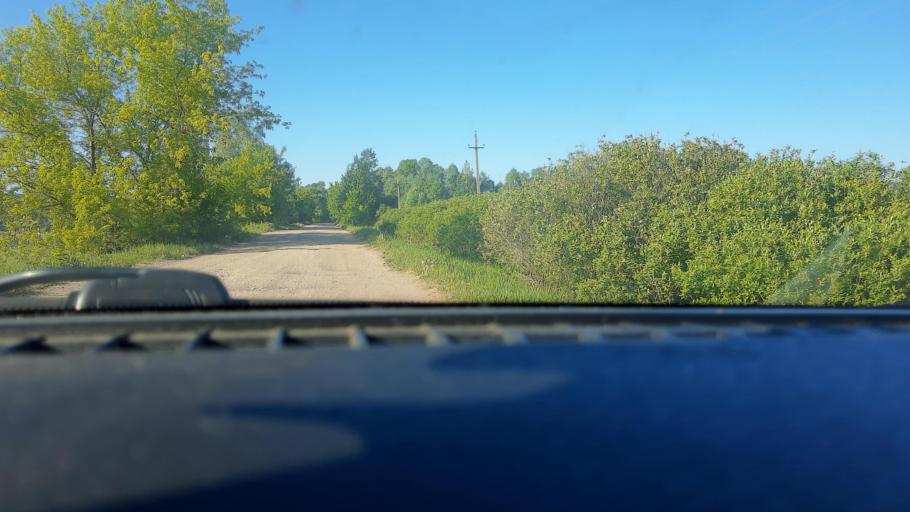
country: RU
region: Bashkortostan
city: Ulukulevo
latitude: 54.5587
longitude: 56.3270
